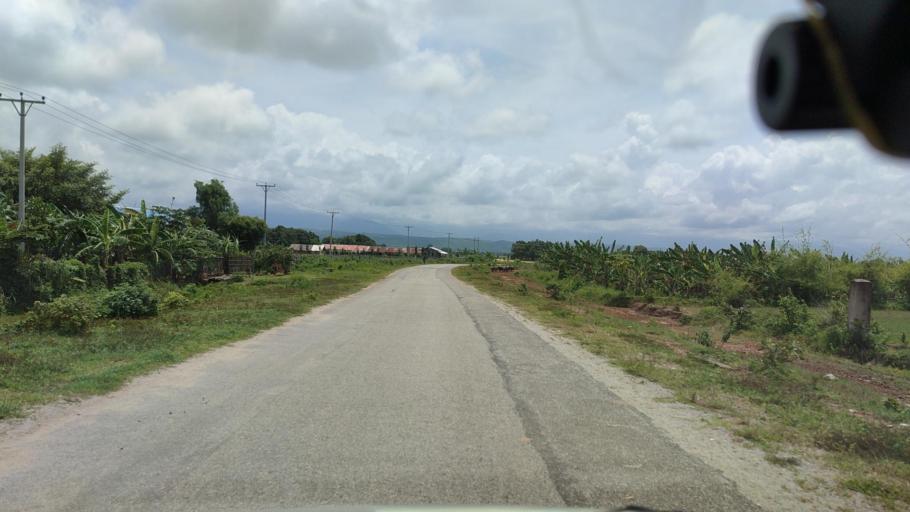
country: MM
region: Bago
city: Taungoo
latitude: 19.1590
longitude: 96.3816
